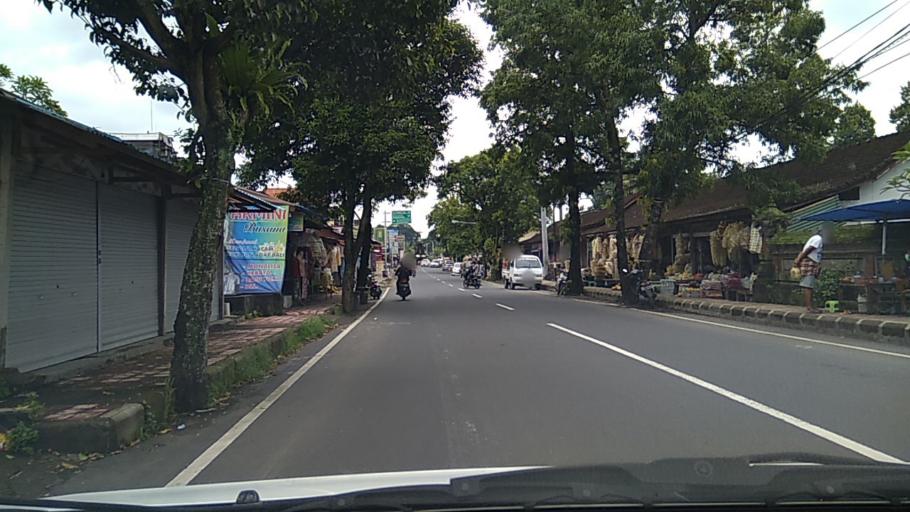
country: ID
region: Bali
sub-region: Kabupaten Gianyar
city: Ubud
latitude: -8.5235
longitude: 115.2907
